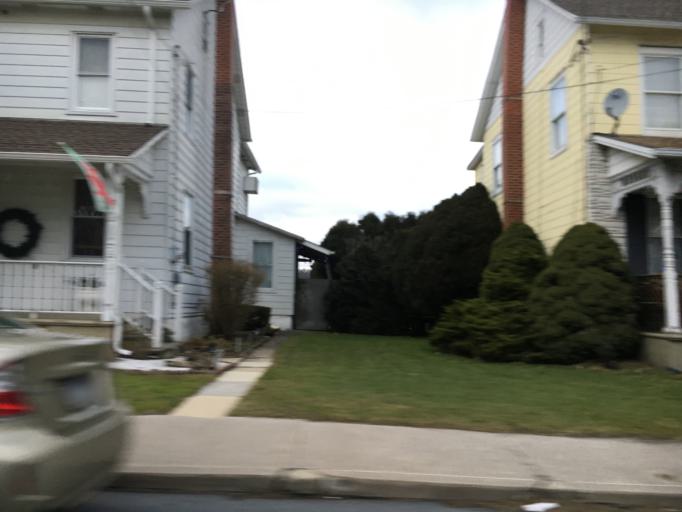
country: US
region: Pennsylvania
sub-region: Lehigh County
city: Egypt
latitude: 40.6799
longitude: -75.5330
